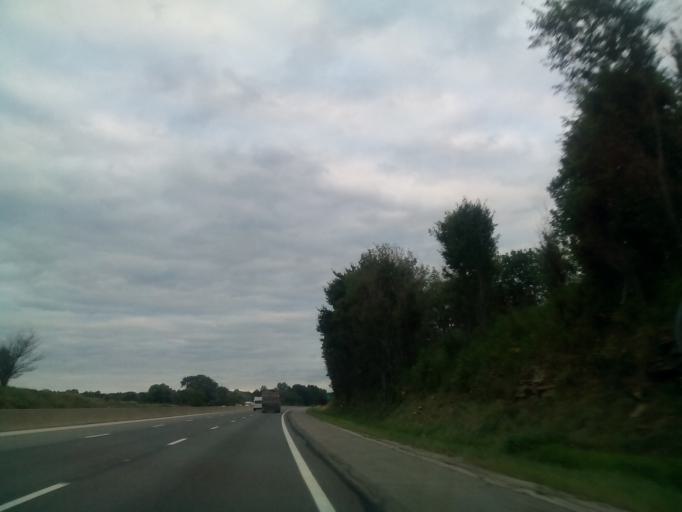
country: US
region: Ohio
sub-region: Trumbull County
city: Newton Falls
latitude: 41.2404
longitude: -80.9904
